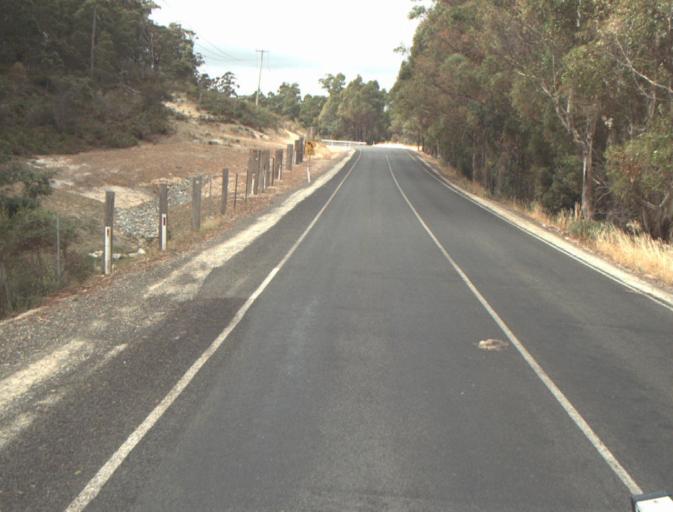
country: AU
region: Tasmania
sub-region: Dorset
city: Bridport
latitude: -41.1651
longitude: 147.2512
